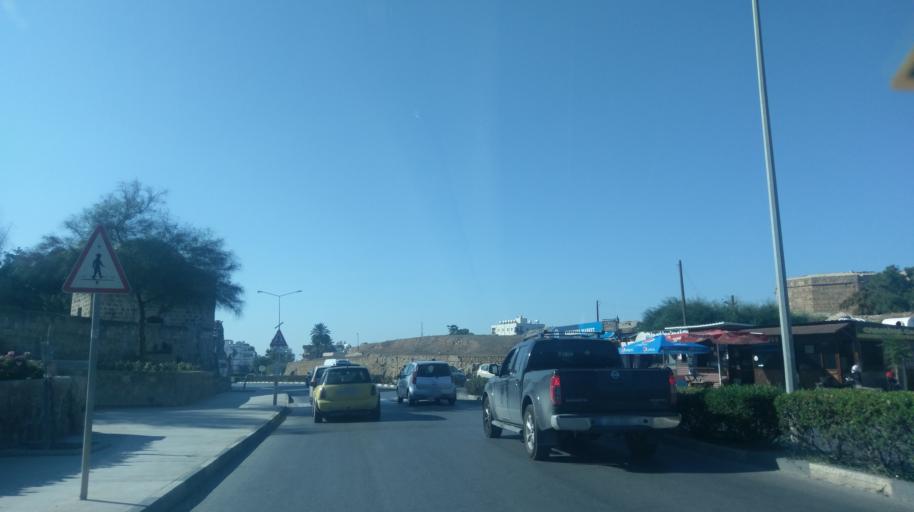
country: CY
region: Ammochostos
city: Famagusta
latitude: 35.1207
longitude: 33.9403
